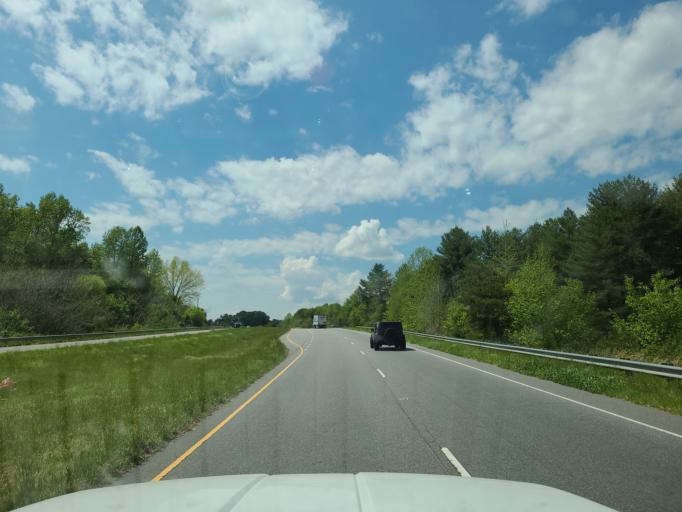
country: US
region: North Carolina
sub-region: Lincoln County
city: Lincolnton
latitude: 35.4245
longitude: -81.3126
